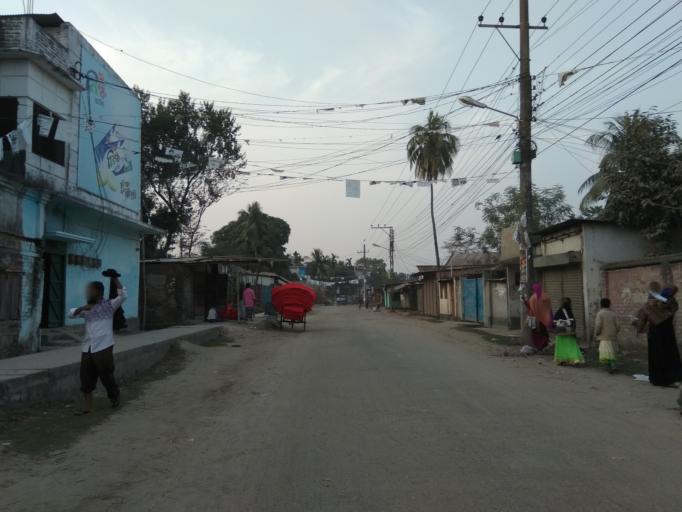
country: BD
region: Rangpur Division
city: Rangpur
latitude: 25.7310
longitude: 89.2625
